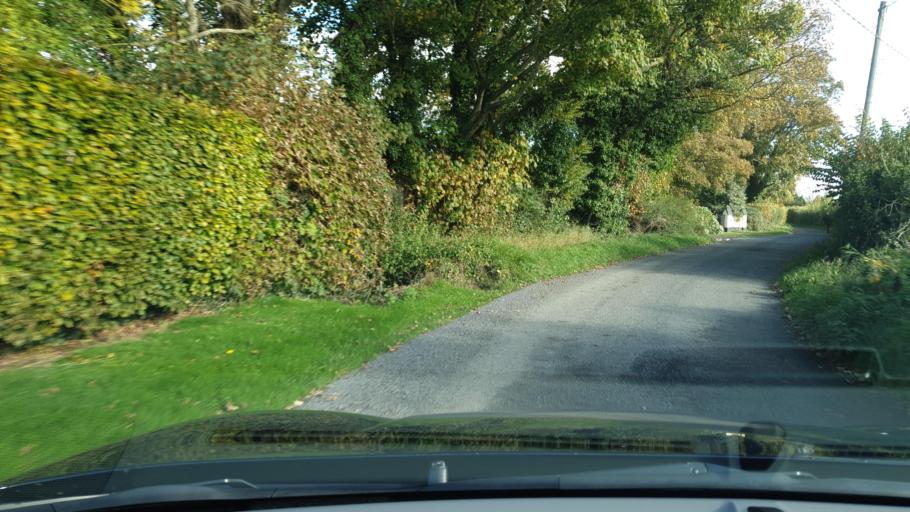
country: IE
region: Leinster
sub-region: Fingal County
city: Swords
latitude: 53.4914
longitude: -6.2572
